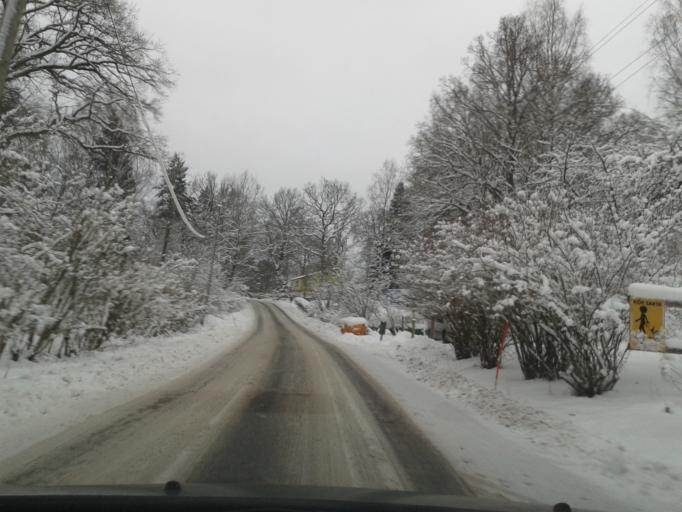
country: SE
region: Stockholm
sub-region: Nacka Kommun
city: Saltsjobaden
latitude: 59.2205
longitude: 18.3040
